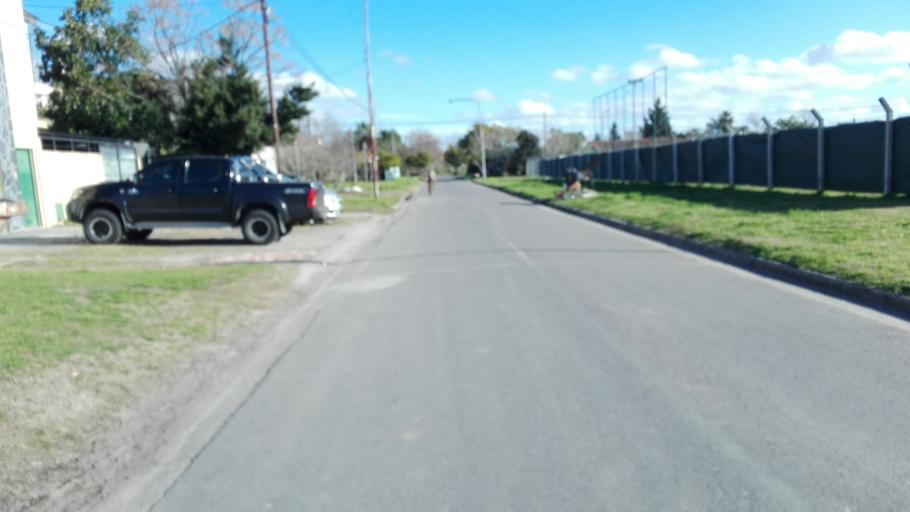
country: AR
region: Buenos Aires
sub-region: Partido de La Plata
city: La Plata
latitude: -34.8806
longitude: -57.9985
